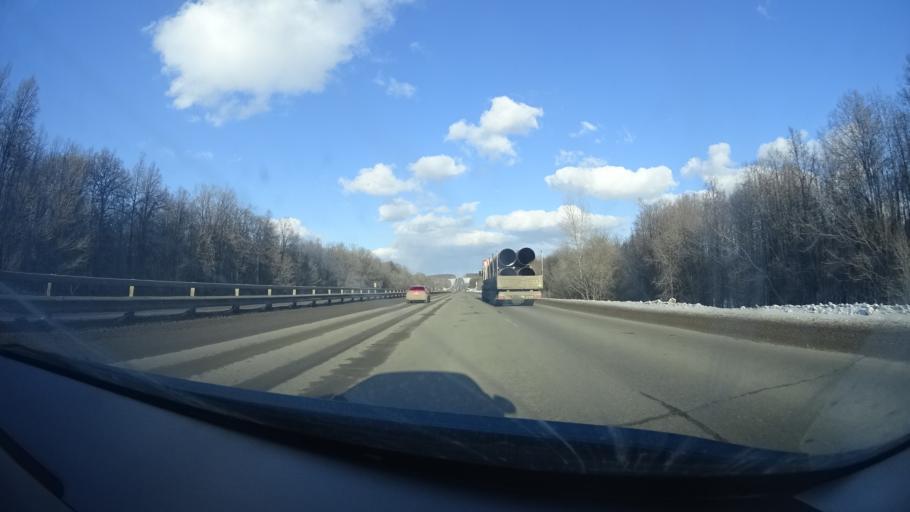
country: RU
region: Bashkortostan
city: Avdon
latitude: 54.6456
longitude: 55.6333
